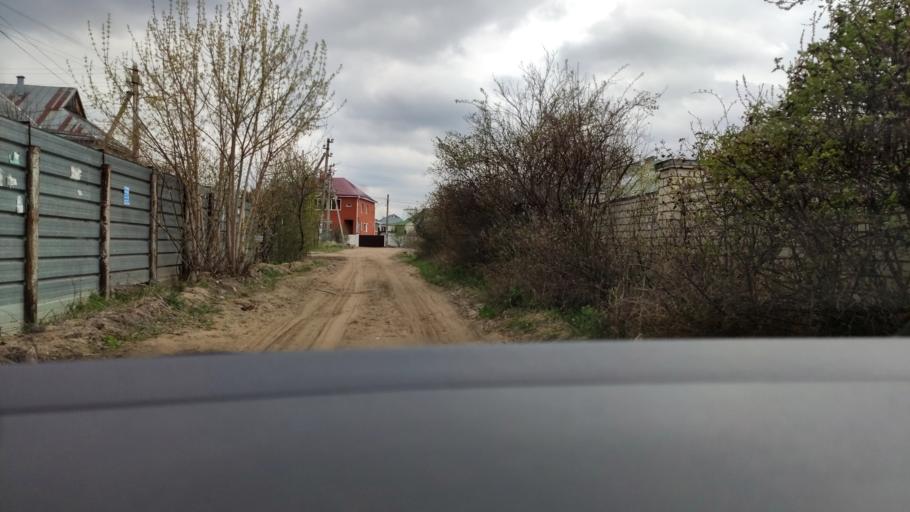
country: RU
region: Voronezj
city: Pridonskoy
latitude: 51.6566
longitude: 39.0915
